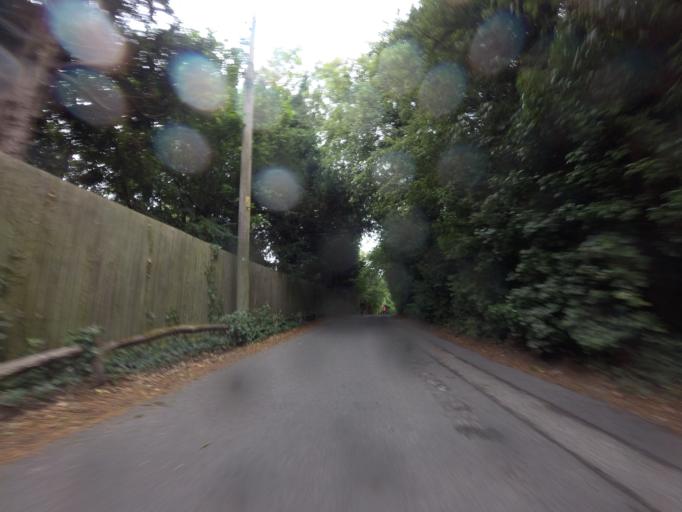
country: GB
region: England
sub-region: Kent
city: Kemsing
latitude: 51.3088
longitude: 0.2280
